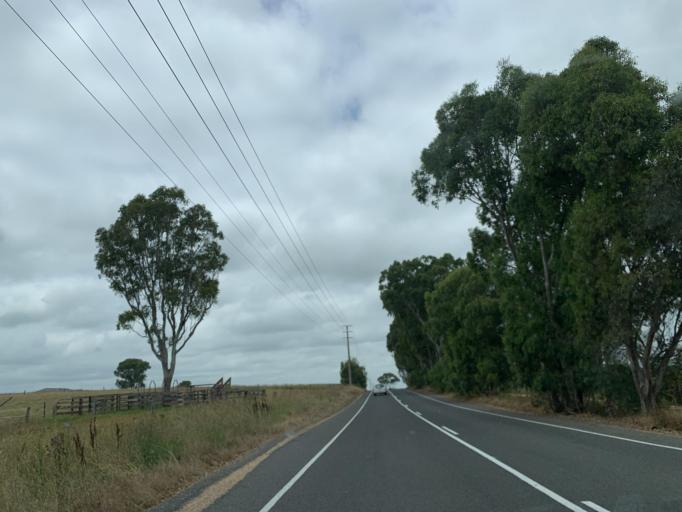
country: AU
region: Victoria
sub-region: Wellington
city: Heyfield
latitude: -37.9860
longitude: 146.8444
